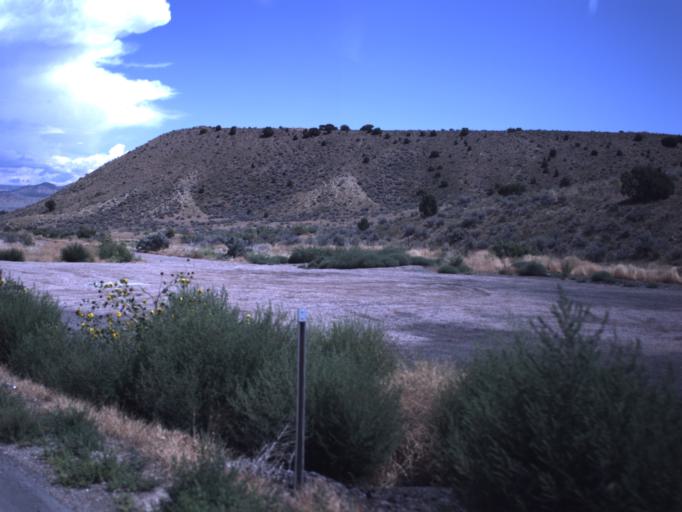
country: US
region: Utah
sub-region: Uintah County
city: Maeser
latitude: 40.4578
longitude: -109.6167
